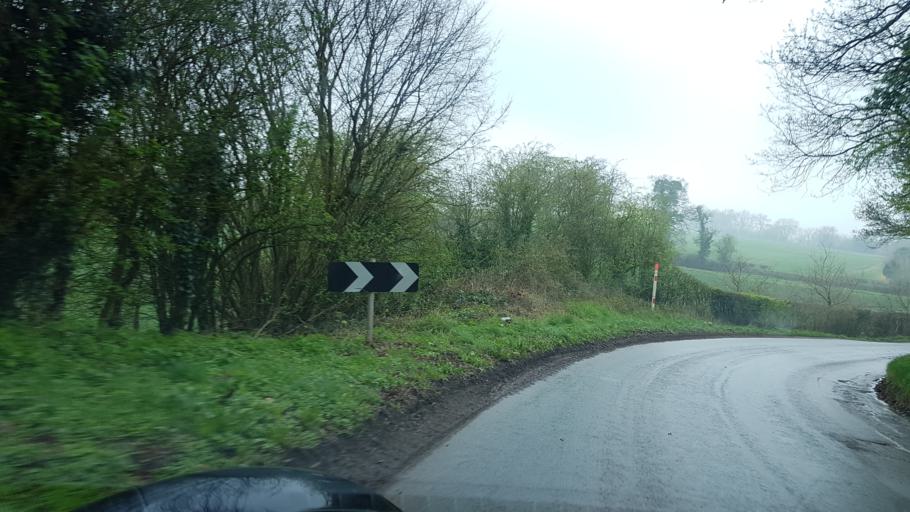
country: GB
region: England
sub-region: Herefordshire
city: Sellack
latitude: 51.9441
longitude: -2.6567
